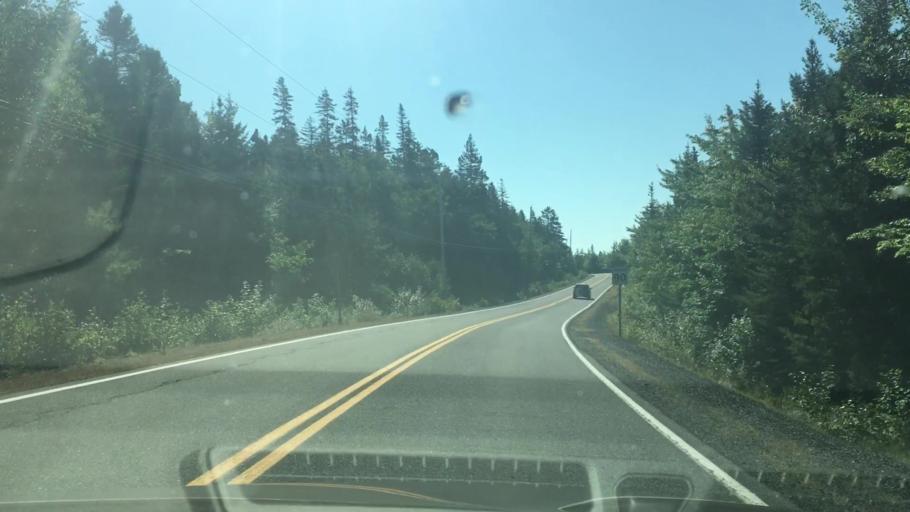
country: CA
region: Nova Scotia
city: Cole Harbour
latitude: 44.8105
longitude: -62.8357
